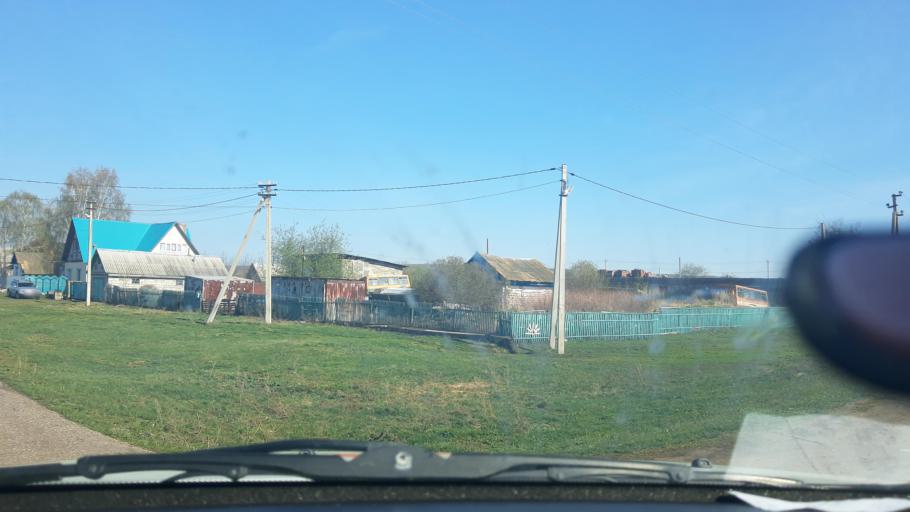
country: RU
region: Bashkortostan
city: Sterlitamak
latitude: 53.5935
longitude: 56.0487
